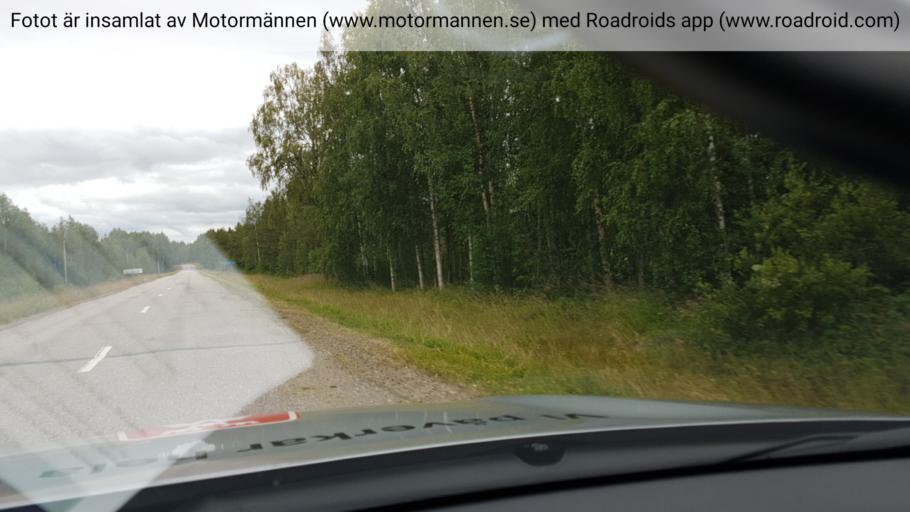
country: SE
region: Norrbotten
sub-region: Overkalix Kommun
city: OEverkalix
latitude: 66.7721
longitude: 22.9008
